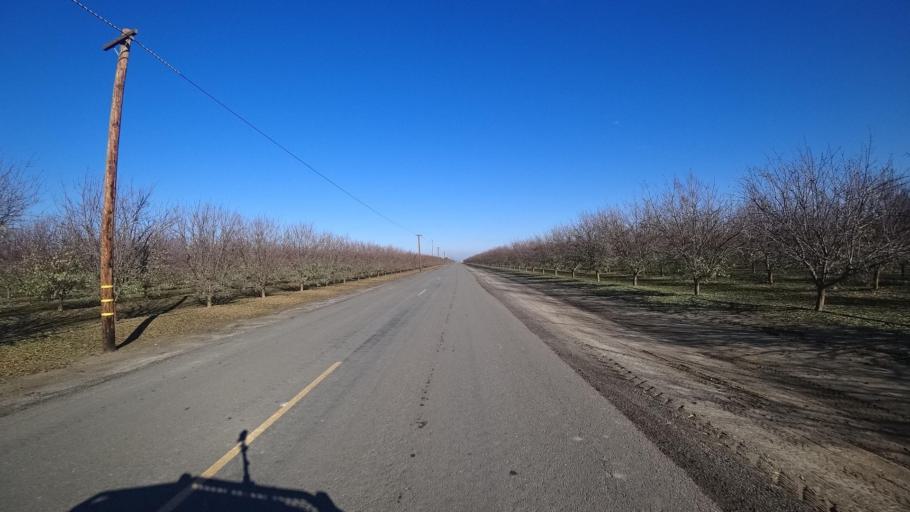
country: US
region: California
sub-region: Kern County
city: Delano
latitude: 35.7414
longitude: -119.3119
